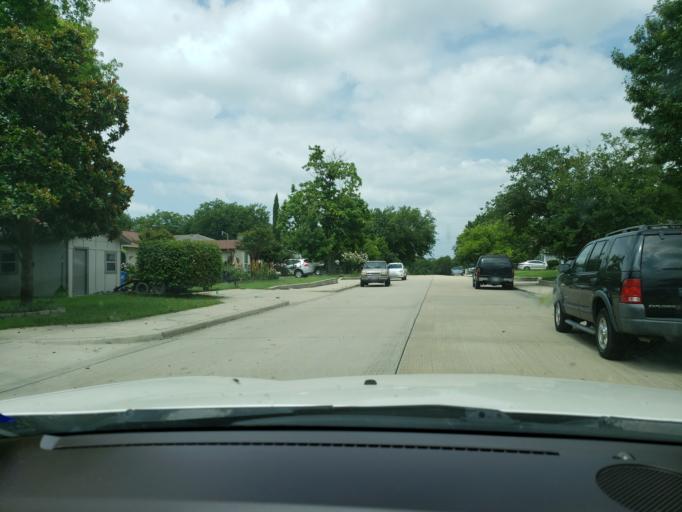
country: US
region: Texas
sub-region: Dallas County
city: Rowlett
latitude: 32.8987
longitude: -96.5676
